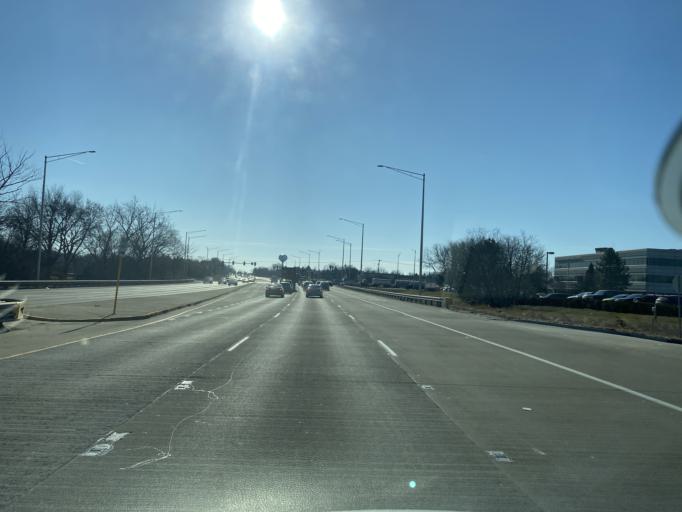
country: US
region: Illinois
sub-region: DuPage County
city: Willowbrook
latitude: 41.7761
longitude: -87.9468
